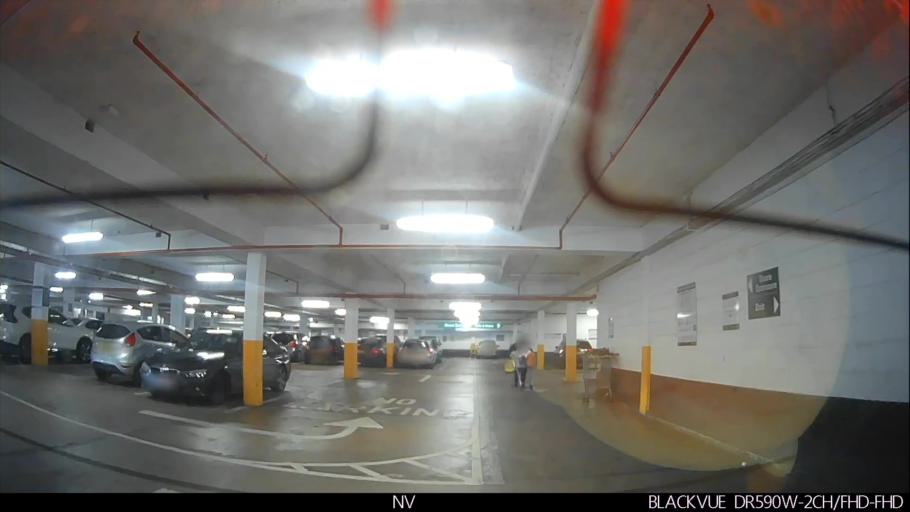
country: GB
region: England
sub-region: City and Borough of Leeds
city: Leeds
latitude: 53.8015
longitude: -1.5457
